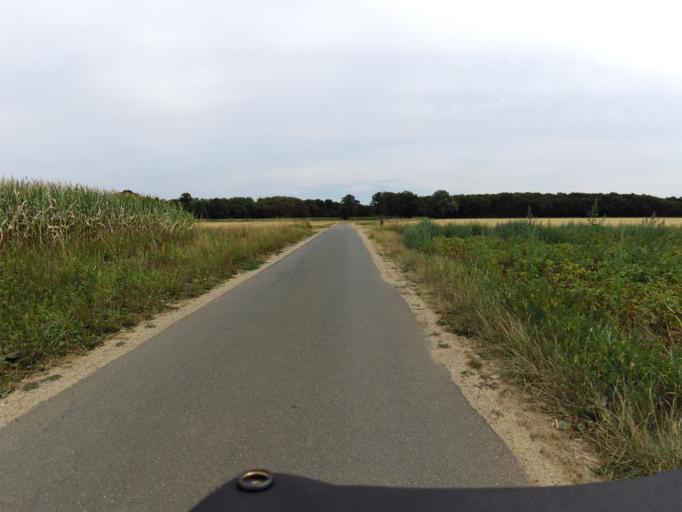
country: DE
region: North Rhine-Westphalia
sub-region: Regierungsbezirk Dusseldorf
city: Weeze
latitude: 51.5851
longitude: 6.1921
